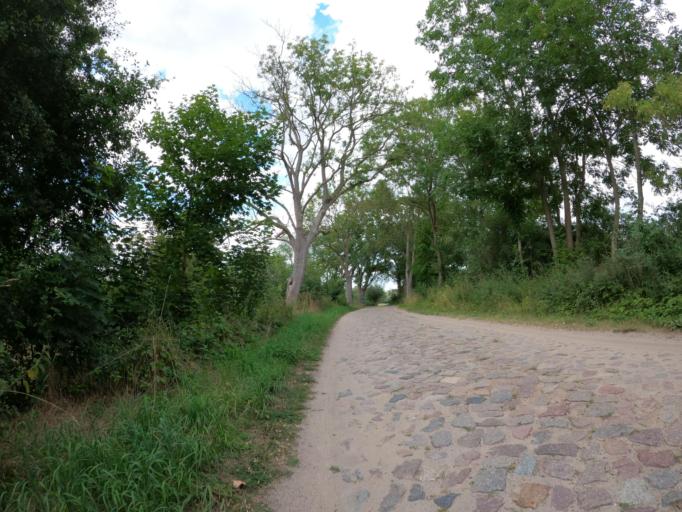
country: DE
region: Mecklenburg-Vorpommern
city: Woldegk
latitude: 53.4049
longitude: 13.6211
